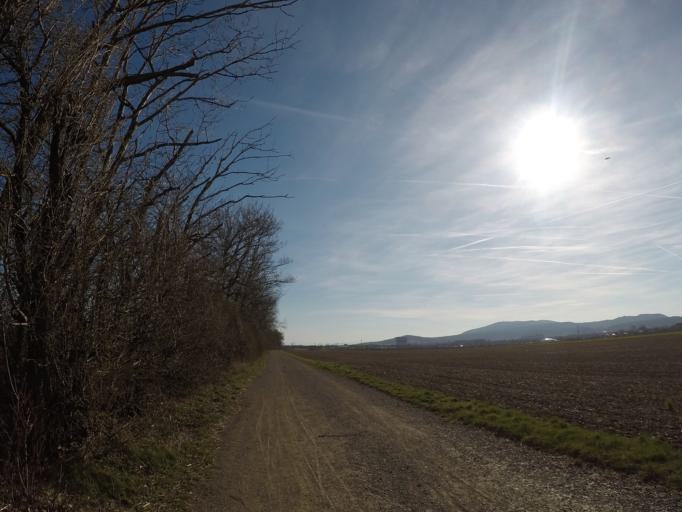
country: AT
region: Lower Austria
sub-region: Politischer Bezirk Modling
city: Vosendorf
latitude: 48.1074
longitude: 16.3322
